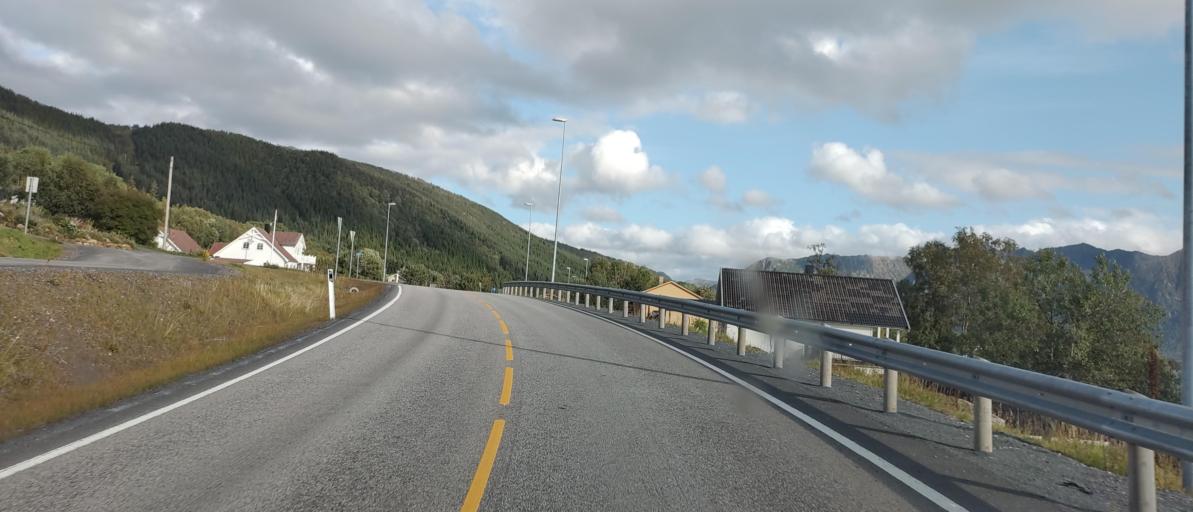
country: NO
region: Nordland
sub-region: Sortland
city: Sortland
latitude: 68.7518
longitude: 15.4762
